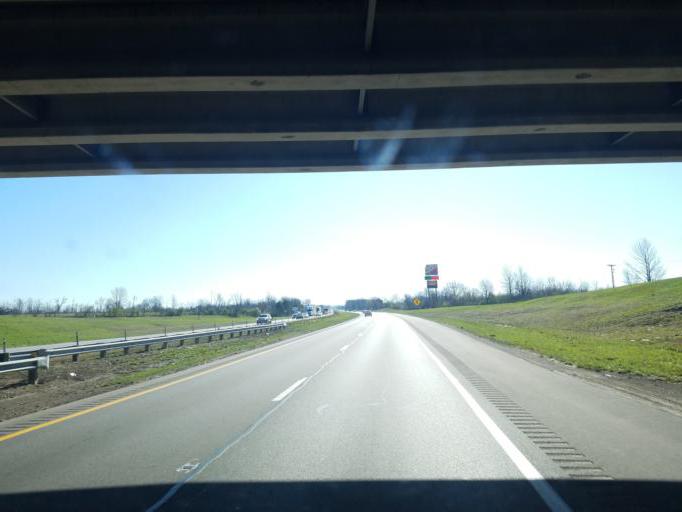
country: US
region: Ohio
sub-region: Fairfield County
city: Millersport
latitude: 39.9452
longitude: -82.6013
